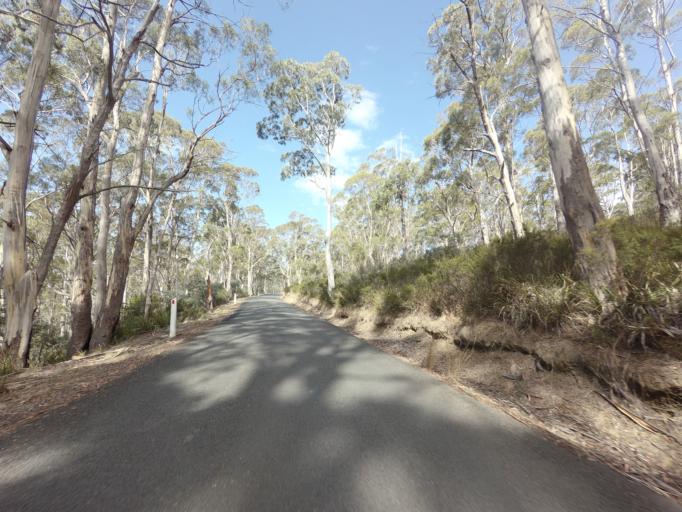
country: AU
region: Tasmania
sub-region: Hobart
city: Dynnyrne
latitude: -42.9207
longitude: 147.2851
